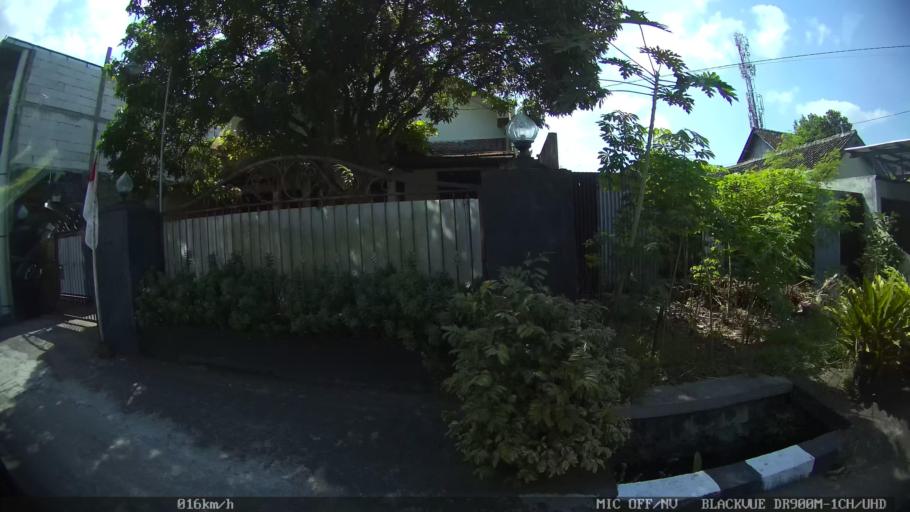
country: ID
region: Daerah Istimewa Yogyakarta
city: Kasihan
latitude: -7.8286
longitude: 110.3725
